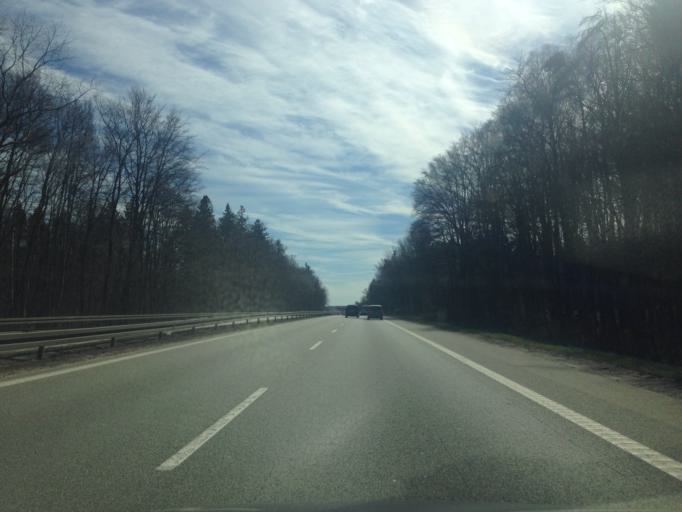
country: PL
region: Pomeranian Voivodeship
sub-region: Gdynia
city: Wielki Kack
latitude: 54.4419
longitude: 18.4896
